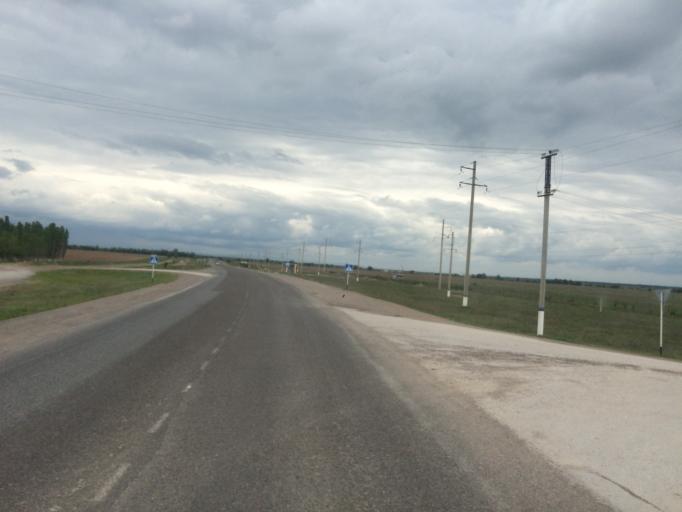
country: KG
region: Chuy
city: Sokuluk
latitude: 43.2464
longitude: 74.3001
